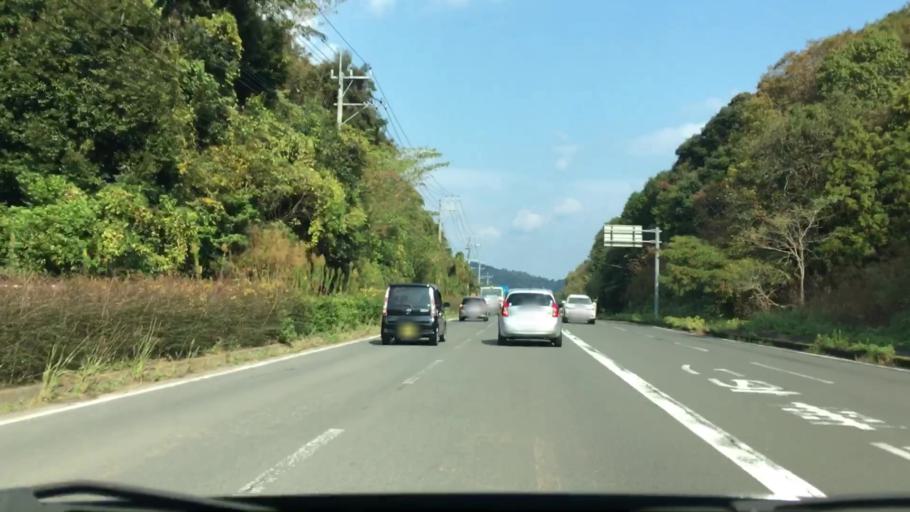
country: JP
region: Nagasaki
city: Sasebo
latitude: 32.9914
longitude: 129.7498
